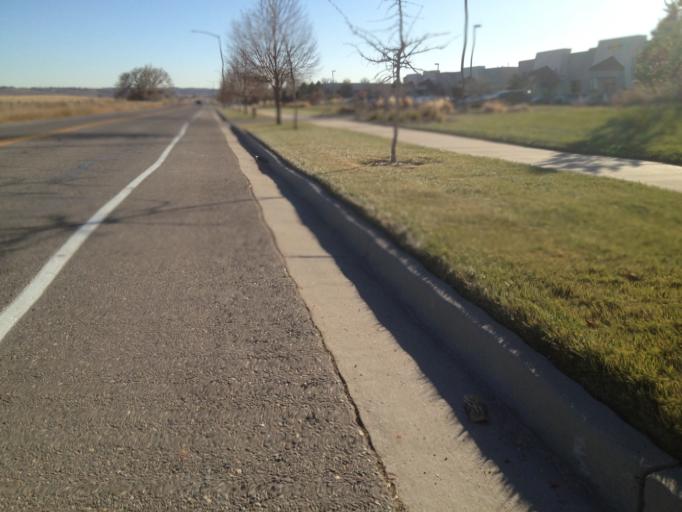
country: US
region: Colorado
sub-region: Boulder County
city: Louisville
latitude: 39.9694
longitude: -105.1094
